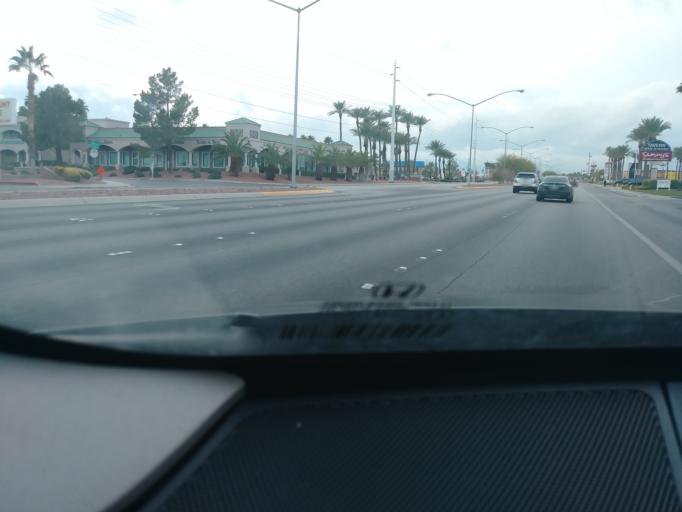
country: US
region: Nevada
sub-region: Clark County
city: Spring Valley
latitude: 36.1442
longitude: -115.2356
